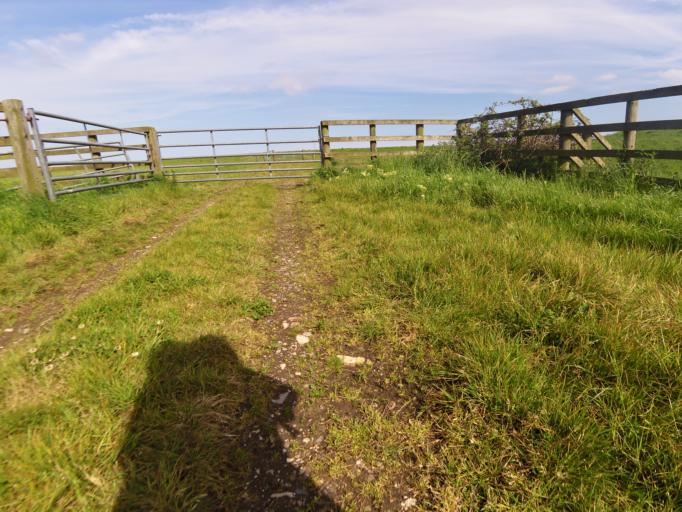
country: GB
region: England
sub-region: Norfolk
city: Great Yarmouth
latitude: 52.6114
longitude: 1.6839
